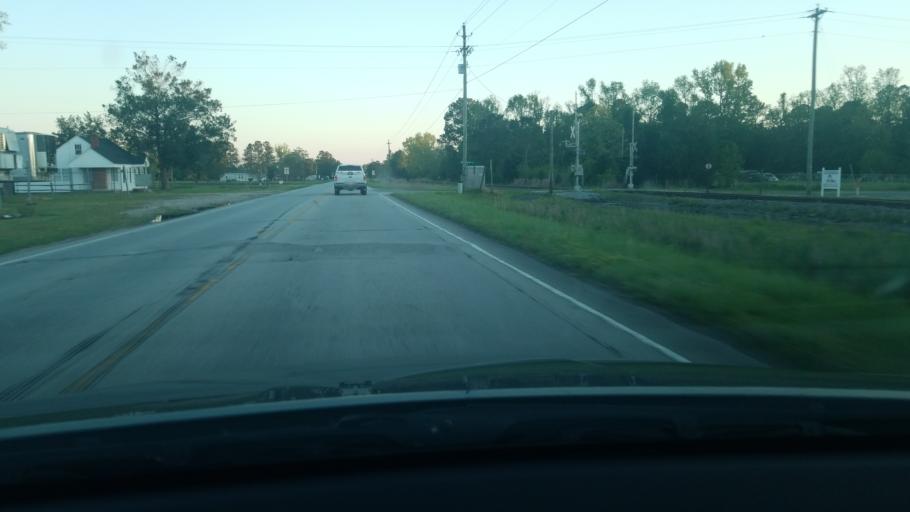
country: US
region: North Carolina
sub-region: Craven County
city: Vanceboro
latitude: 35.3493
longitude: -77.1509
